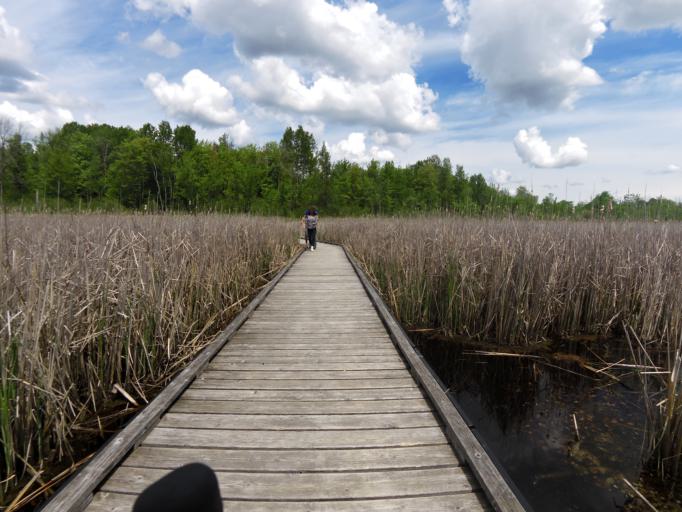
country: CA
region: Ontario
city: Ottawa
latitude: 45.3926
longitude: -75.5091
